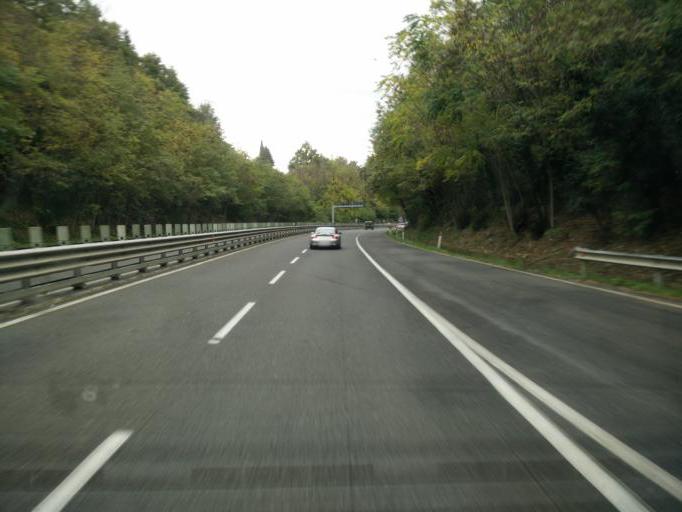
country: IT
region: Tuscany
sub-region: Province of Florence
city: Sambuca
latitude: 43.5539
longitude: 11.2103
